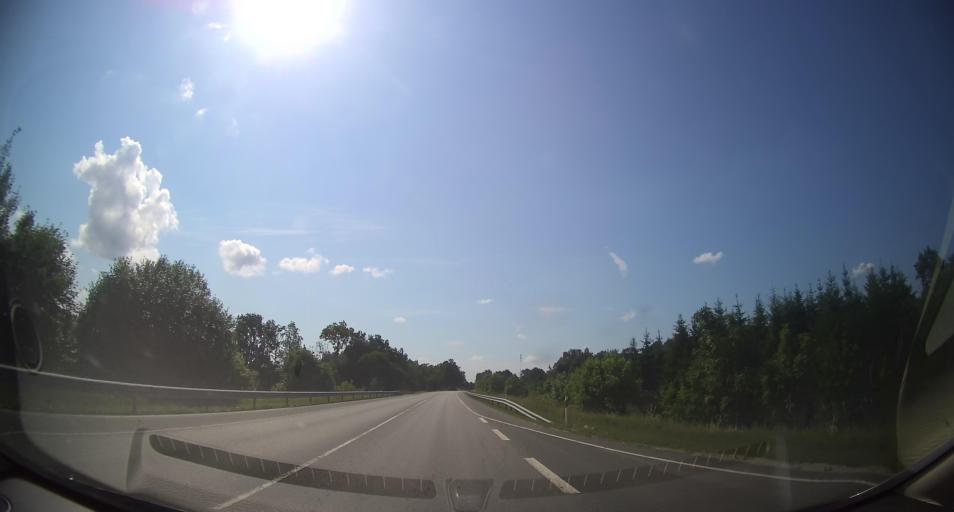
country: EE
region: Raplamaa
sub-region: Kohila vald
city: Kohila
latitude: 59.1066
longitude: 24.7968
